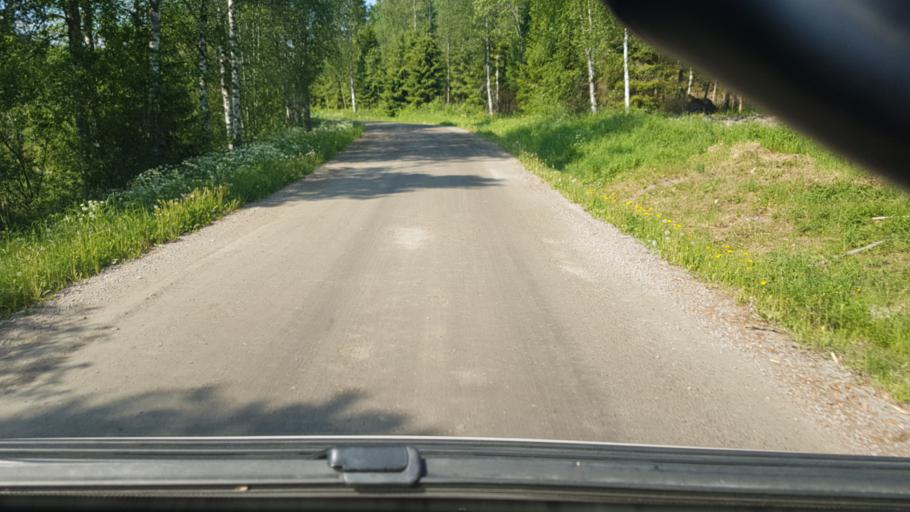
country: SE
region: Vaermland
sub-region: Eda Kommun
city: Amotfors
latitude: 59.7780
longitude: 12.4381
